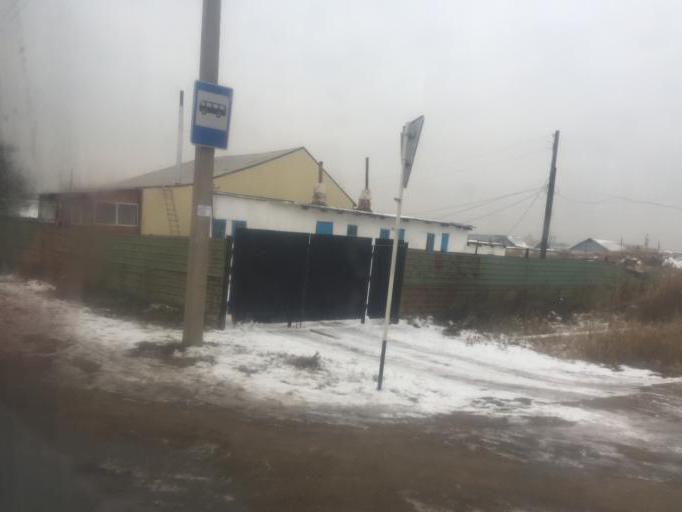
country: KZ
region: Astana Qalasy
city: Astana
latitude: 51.2019
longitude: 71.4108
